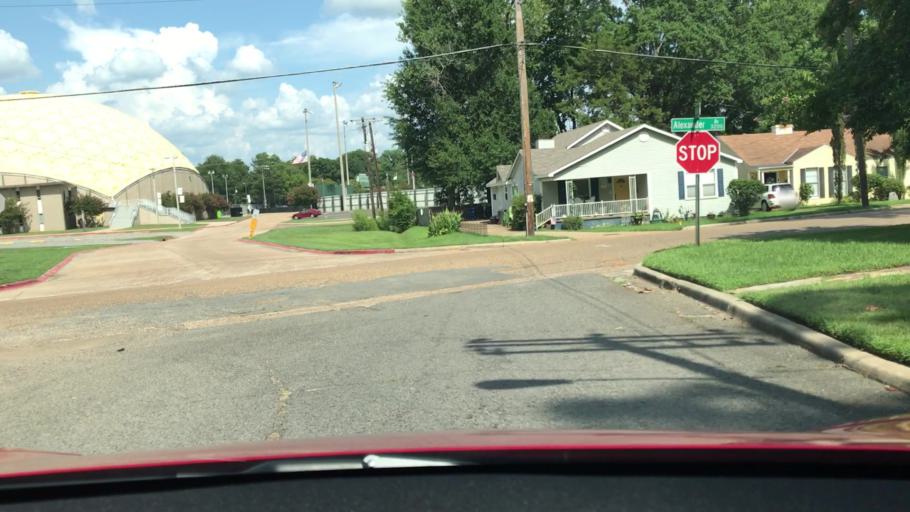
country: US
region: Louisiana
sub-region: Bossier Parish
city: Bossier City
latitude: 32.4804
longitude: -93.7317
